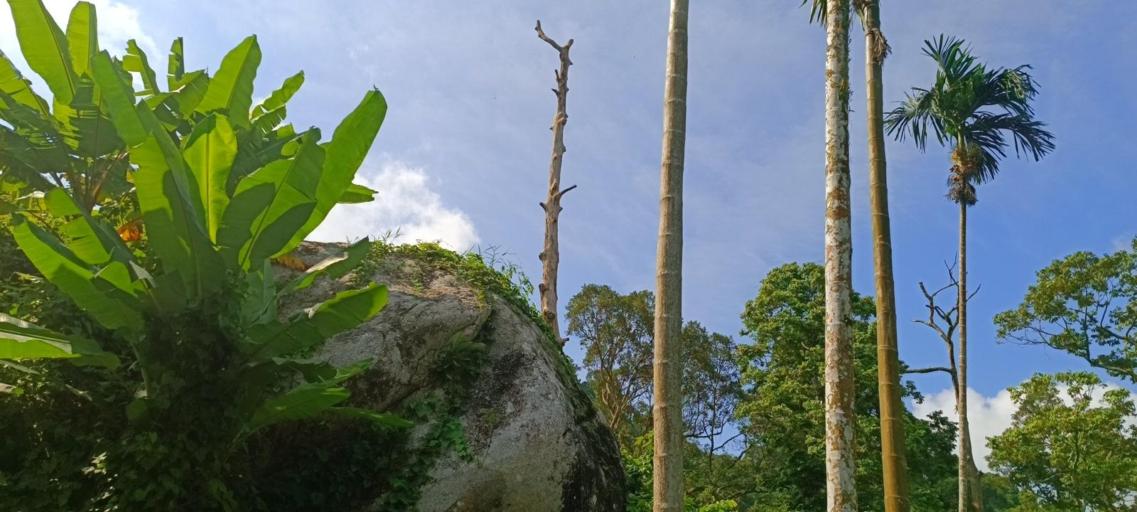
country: MY
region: Penang
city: Bukit Mertajam
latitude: 5.3676
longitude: 100.4786
